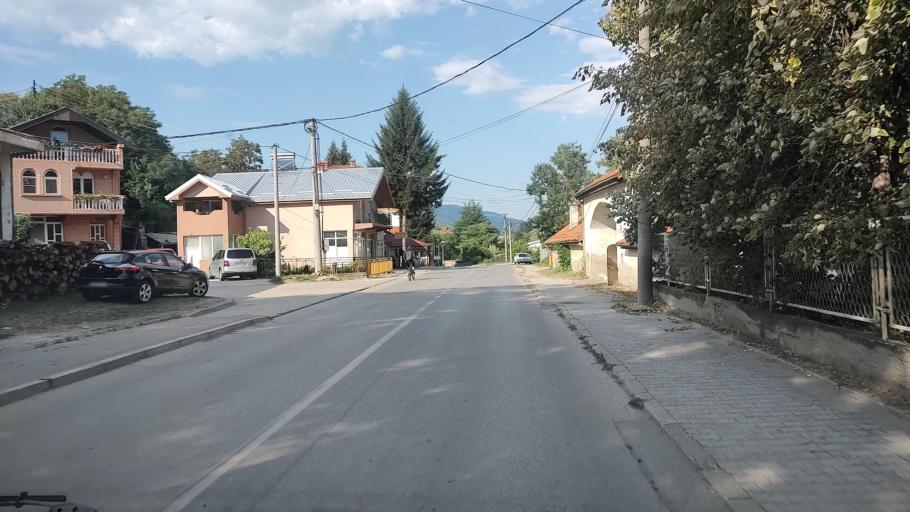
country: MK
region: Kriva Palanka
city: Kriva Palanka
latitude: 42.1963
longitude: 22.3203
